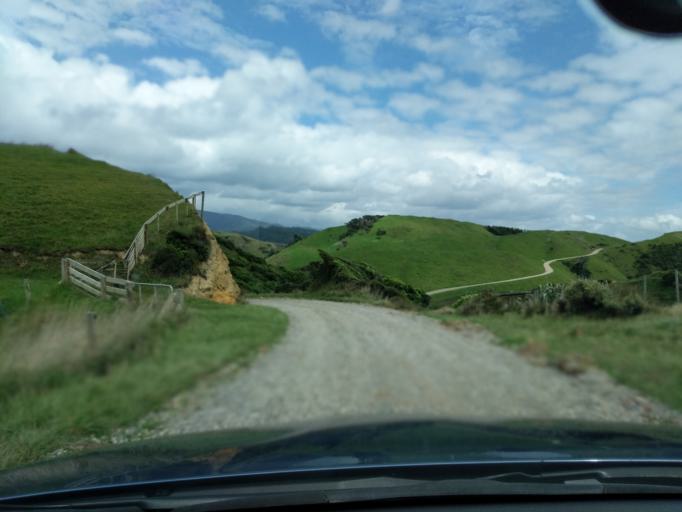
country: NZ
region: Tasman
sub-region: Tasman District
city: Takaka
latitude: -40.6694
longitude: 172.3995
